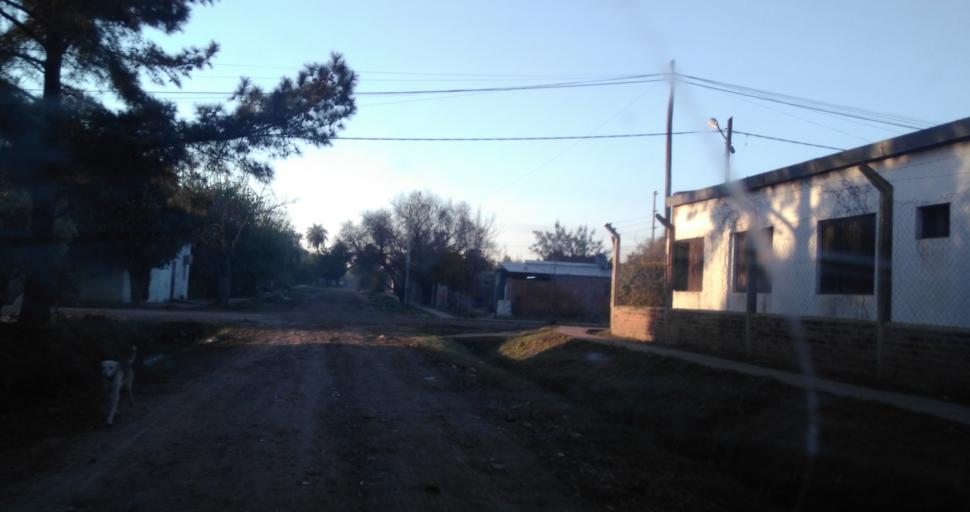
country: AR
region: Chaco
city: Fontana
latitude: -27.4288
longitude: -59.0177
